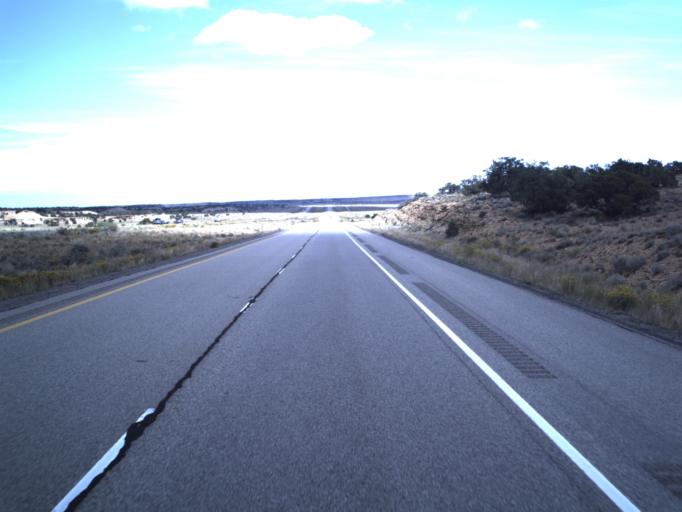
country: US
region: Utah
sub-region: Emery County
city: Castle Dale
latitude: 38.8685
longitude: -110.6998
